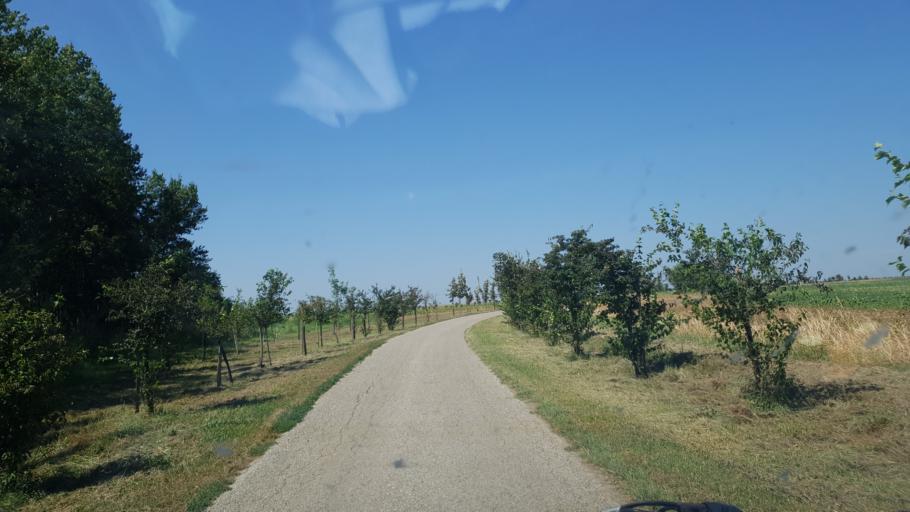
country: RS
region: Autonomna Pokrajina Vojvodina
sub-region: Juznobacki Okrug
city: Kovilj
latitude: 45.2069
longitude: 20.0632
